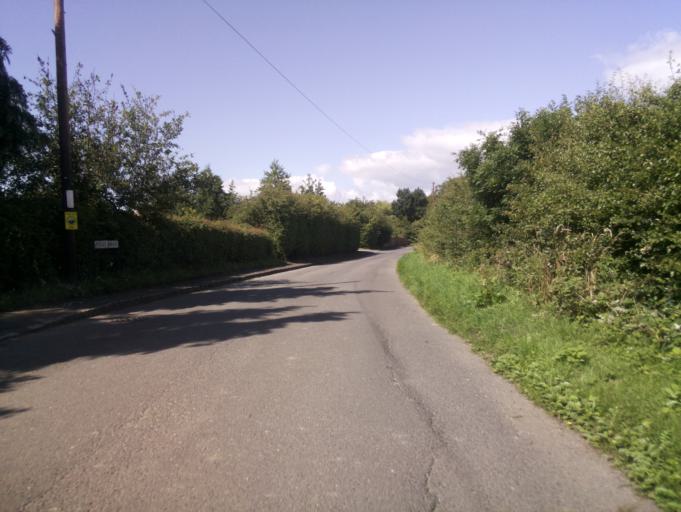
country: GB
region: England
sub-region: Northamptonshire
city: Deanshanger
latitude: 51.9953
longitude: -0.9082
